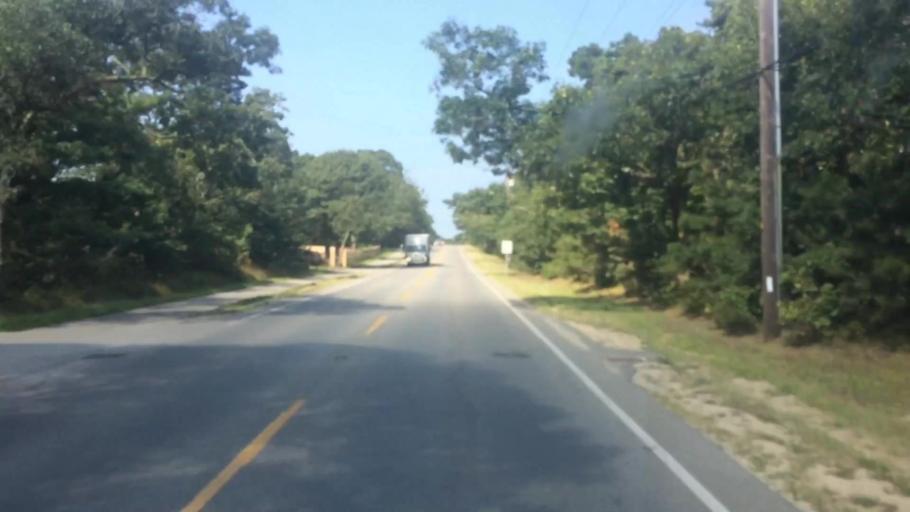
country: US
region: Massachusetts
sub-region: Dukes County
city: Edgartown
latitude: 41.3975
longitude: -70.5395
